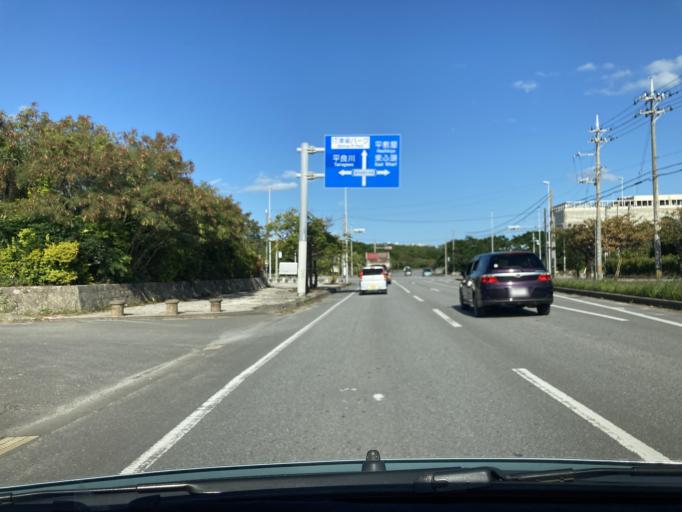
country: JP
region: Okinawa
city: Katsuren-haebaru
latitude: 26.3411
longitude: 127.8570
